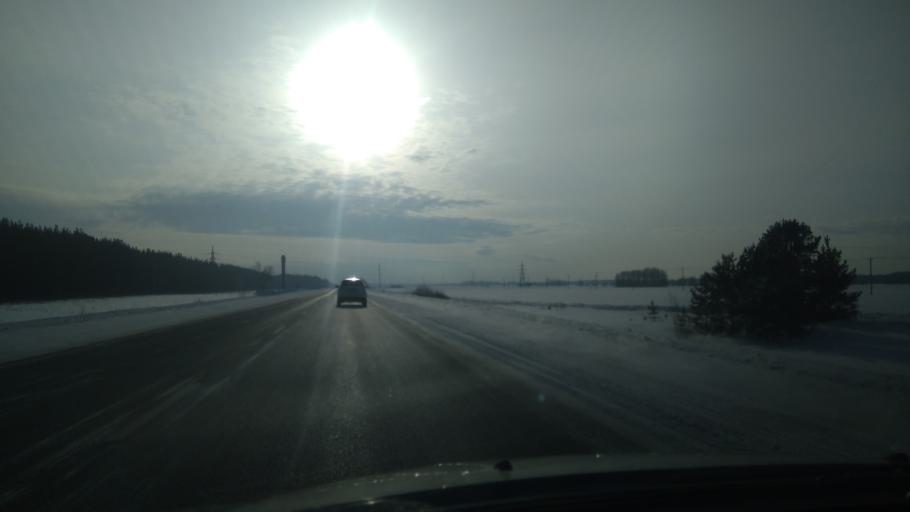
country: RU
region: Sverdlovsk
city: Sukhoy Log
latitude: 56.8686
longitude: 62.0467
